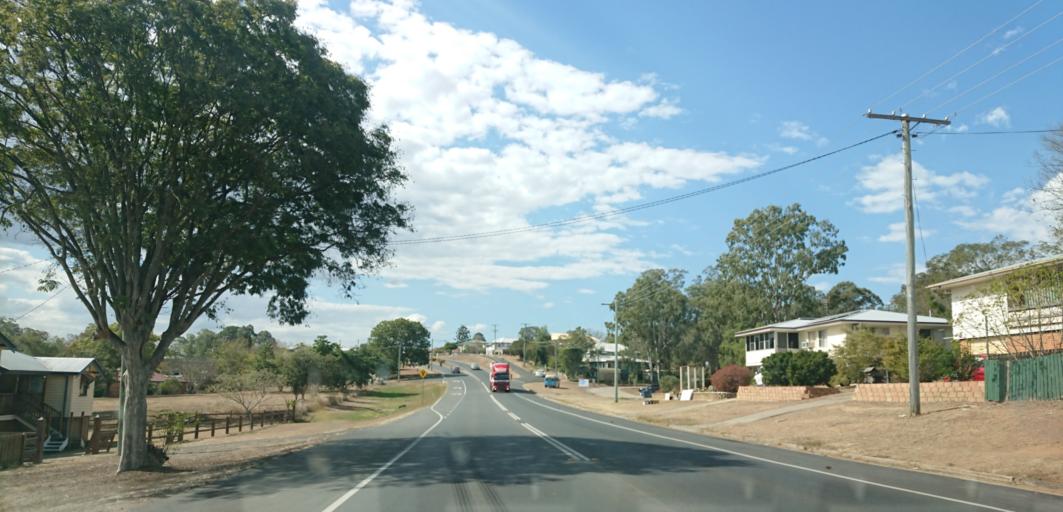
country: AU
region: Queensland
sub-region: Lockyer Valley
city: Gatton
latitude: -27.5666
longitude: 152.2725
